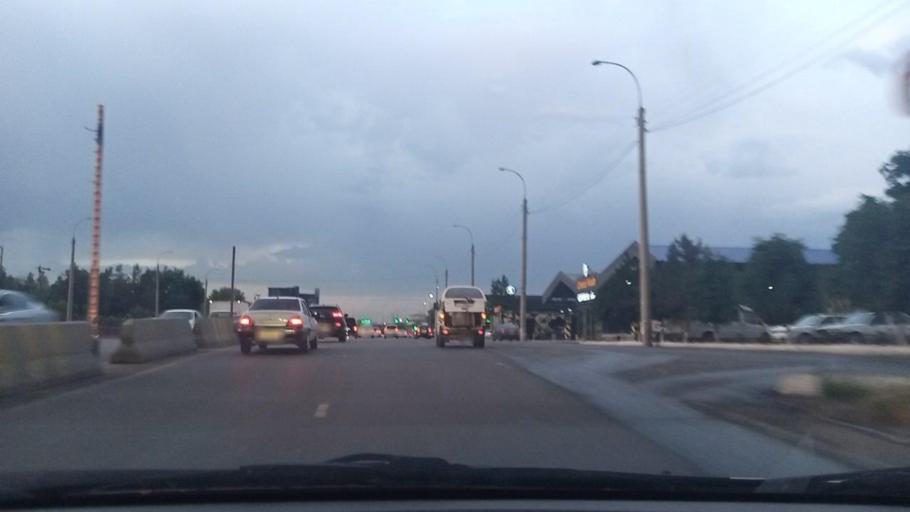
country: UZ
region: Toshkent Shahri
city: Tashkent
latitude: 41.2939
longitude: 69.2895
